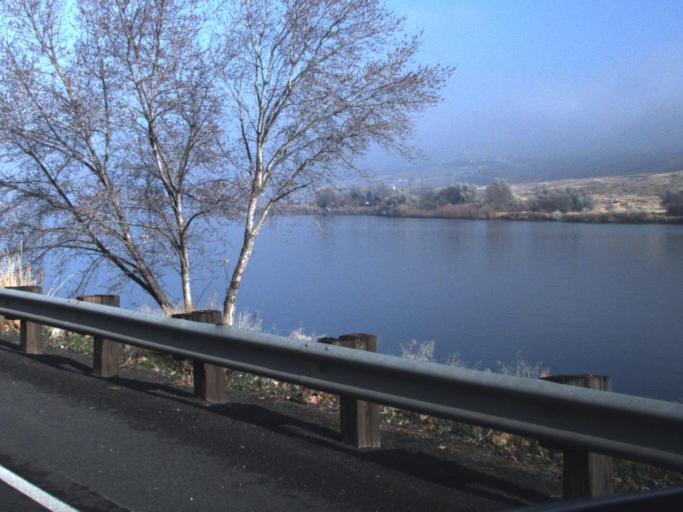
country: US
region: Washington
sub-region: Asotin County
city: Clarkston Heights-Vineland
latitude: 46.3647
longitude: -117.0646
